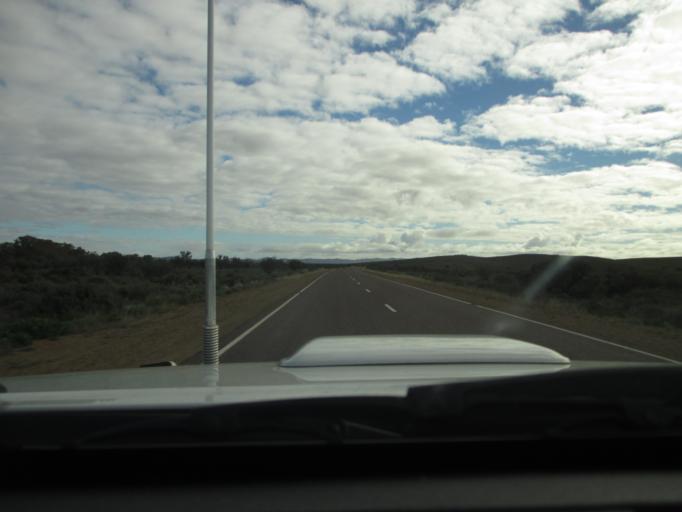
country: AU
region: South Australia
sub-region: Flinders Ranges
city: Quorn
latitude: -32.3669
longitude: 138.4974
